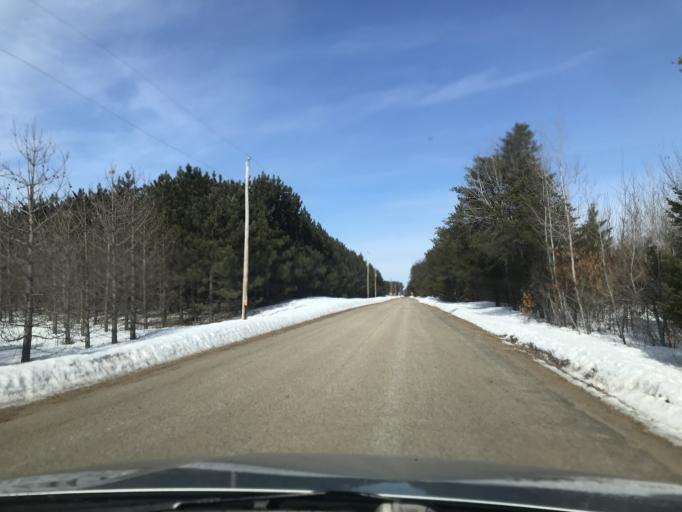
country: US
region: Wisconsin
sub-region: Marinette County
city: Peshtigo
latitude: 45.2143
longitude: -87.9626
